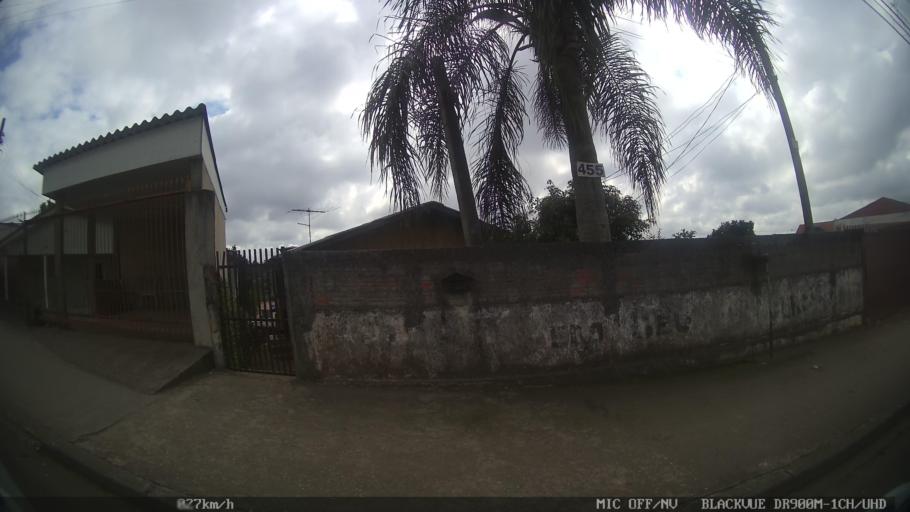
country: BR
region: Parana
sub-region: Almirante Tamandare
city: Almirante Tamandare
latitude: -25.3539
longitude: -49.2588
